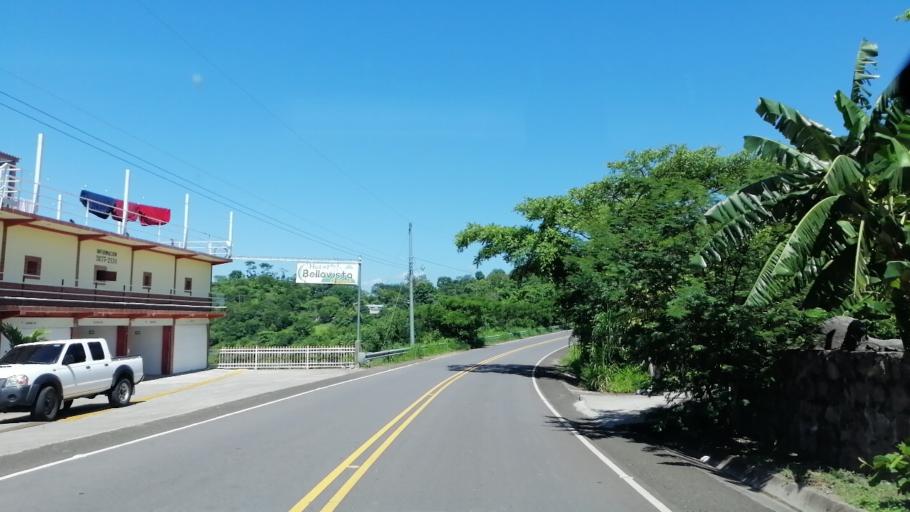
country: SV
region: Morazan
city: Cacaopera
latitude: 13.8094
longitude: -88.1527
